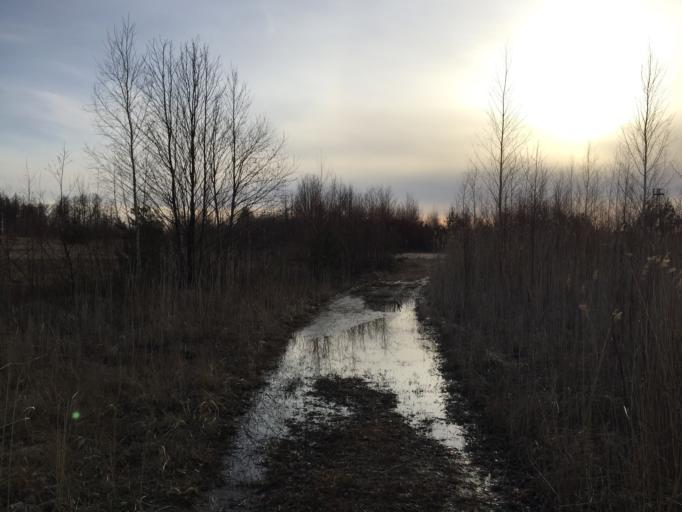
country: LV
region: Salacgrivas
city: Ainazi
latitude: 57.8691
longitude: 24.3553
